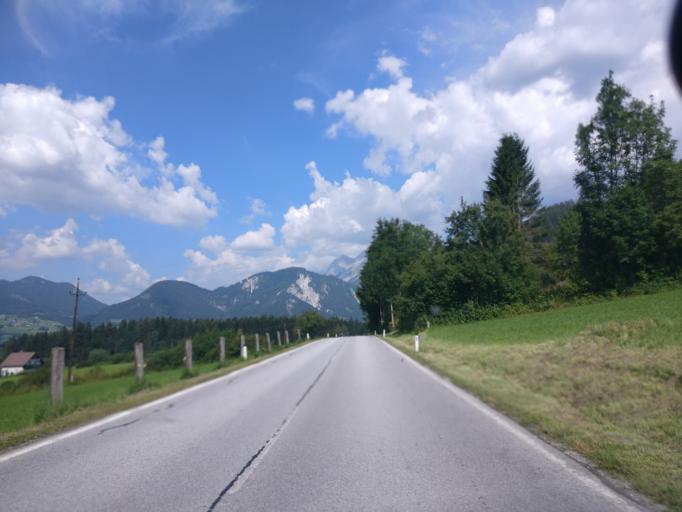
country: AT
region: Styria
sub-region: Politischer Bezirk Liezen
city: Admont
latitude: 47.5754
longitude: 14.4765
